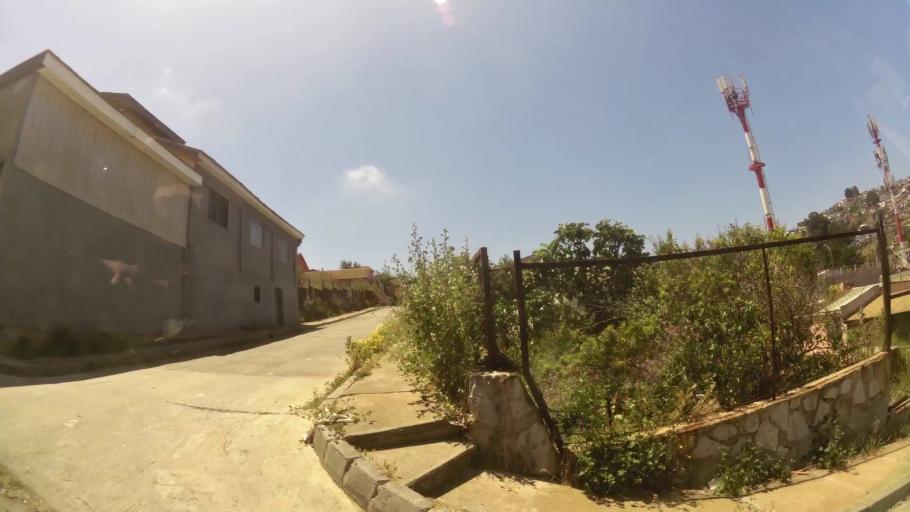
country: CL
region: Valparaiso
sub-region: Provincia de Valparaiso
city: Valparaiso
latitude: -33.0317
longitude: -71.6490
